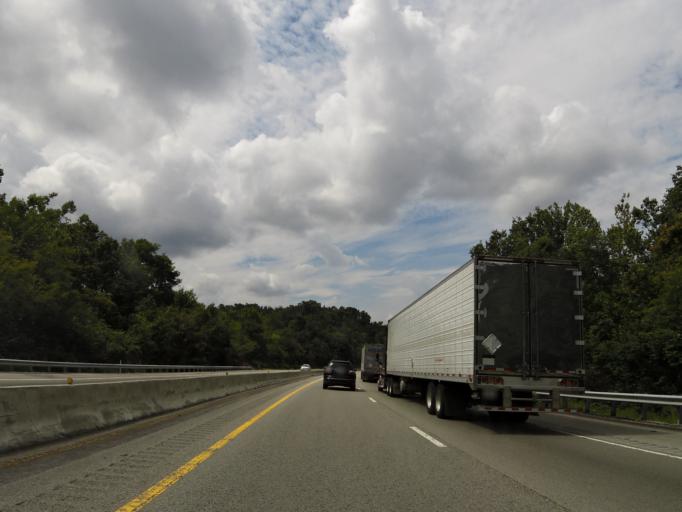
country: US
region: Tennessee
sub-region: Putnam County
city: Monterey
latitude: 36.1297
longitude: -85.3486
